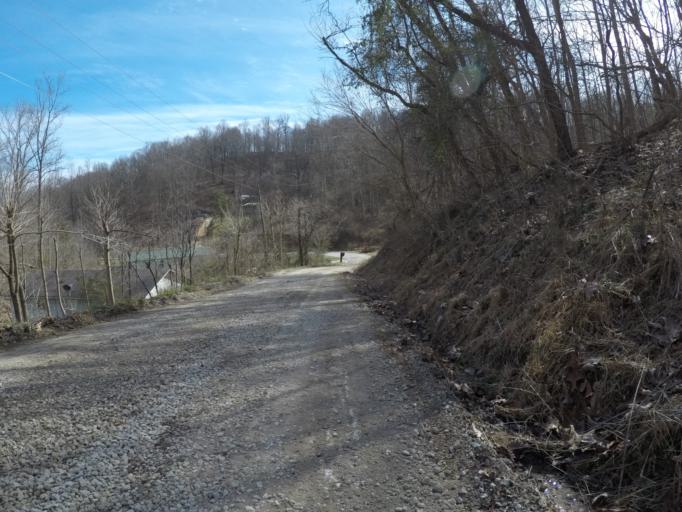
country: US
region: West Virginia
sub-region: Wayne County
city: Ceredo
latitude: 38.3458
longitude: -82.5479
